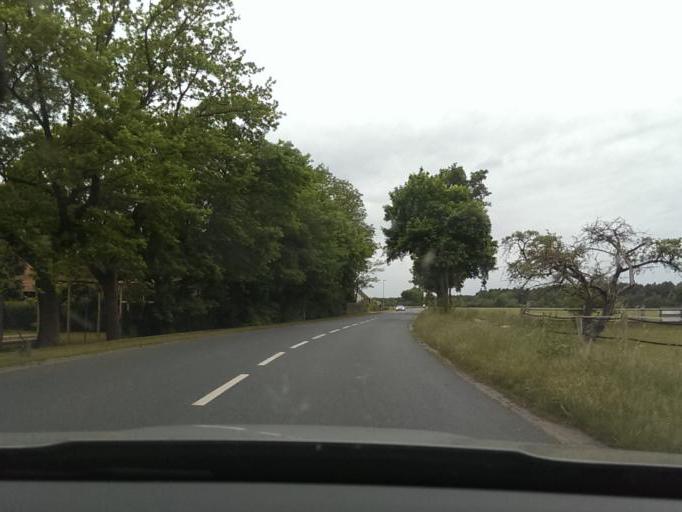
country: DE
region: Lower Saxony
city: Wietze
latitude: 52.6778
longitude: 9.7524
